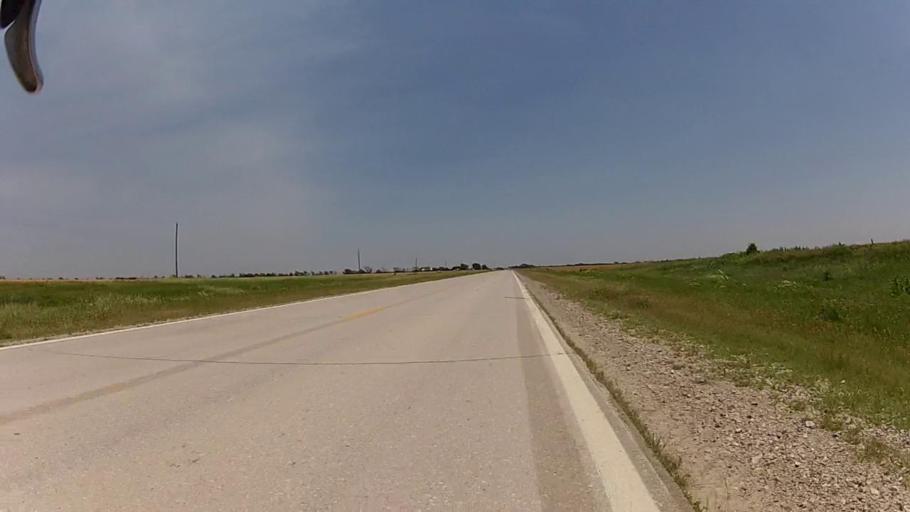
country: US
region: Kansas
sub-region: Sumner County
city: Wellington
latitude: 37.0568
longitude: -97.3820
